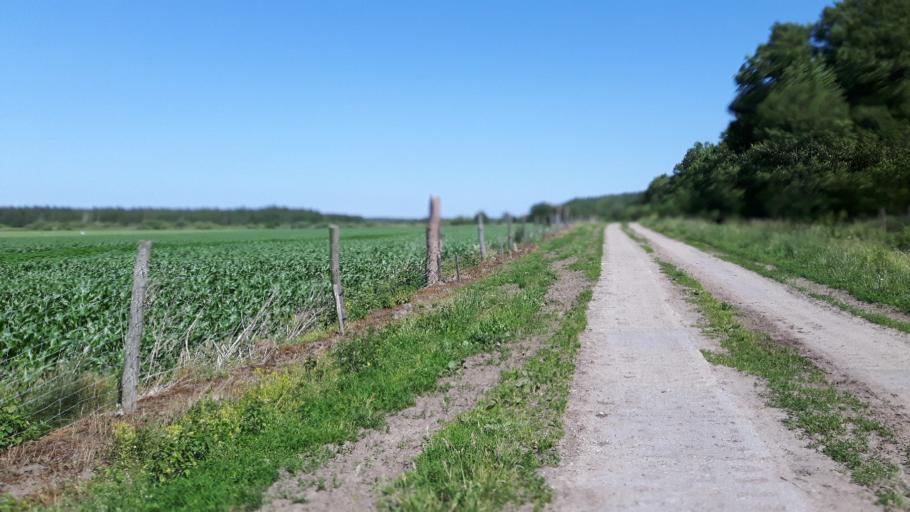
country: PL
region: Pomeranian Voivodeship
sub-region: Powiat slupski
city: Glowczyce
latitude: 54.6409
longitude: 17.3801
